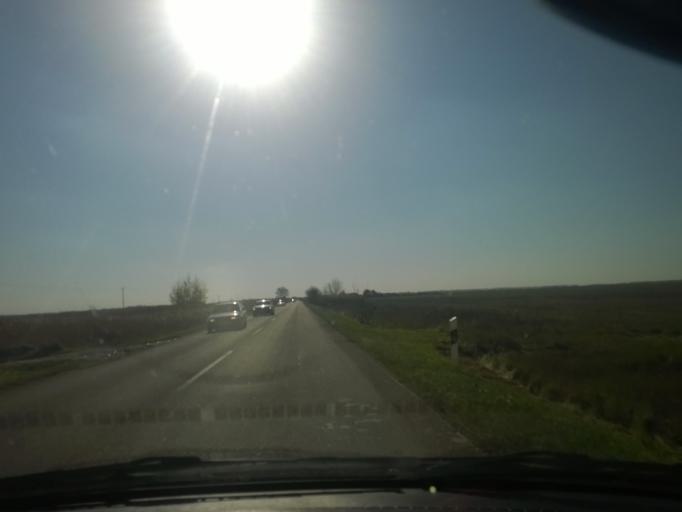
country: HU
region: Csongrad
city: Hodmezovasarhely
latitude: 46.5229
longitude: 20.3121
